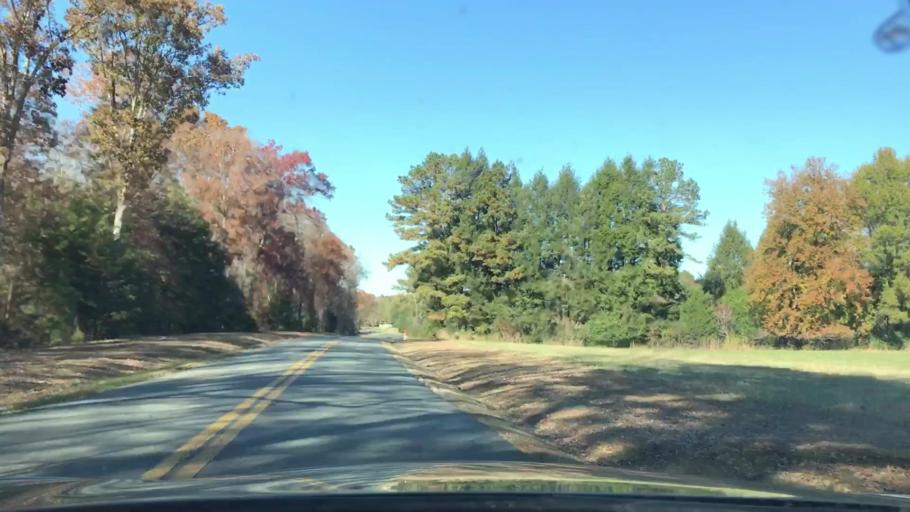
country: US
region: Virginia
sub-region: Henrico County
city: Short Pump
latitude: 37.6460
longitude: -77.7173
